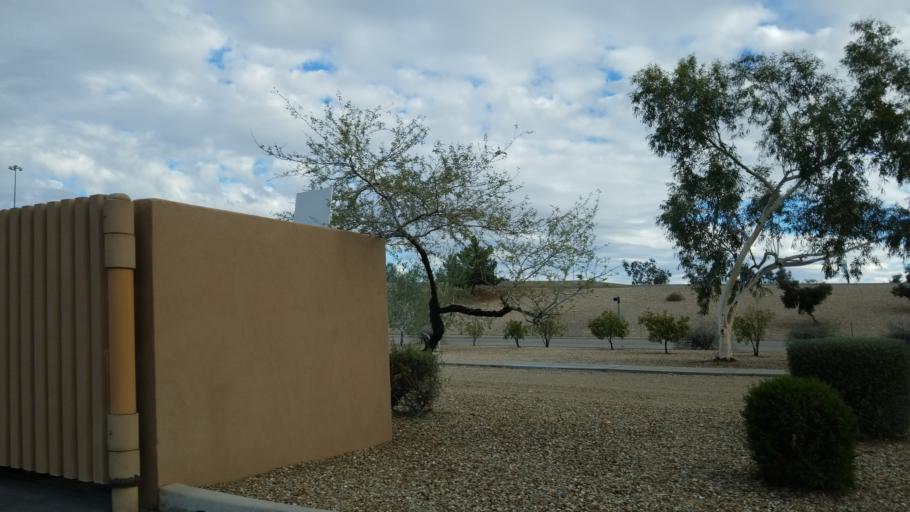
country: US
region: Arizona
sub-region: Maricopa County
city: Glendale
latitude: 33.6700
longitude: -112.1188
